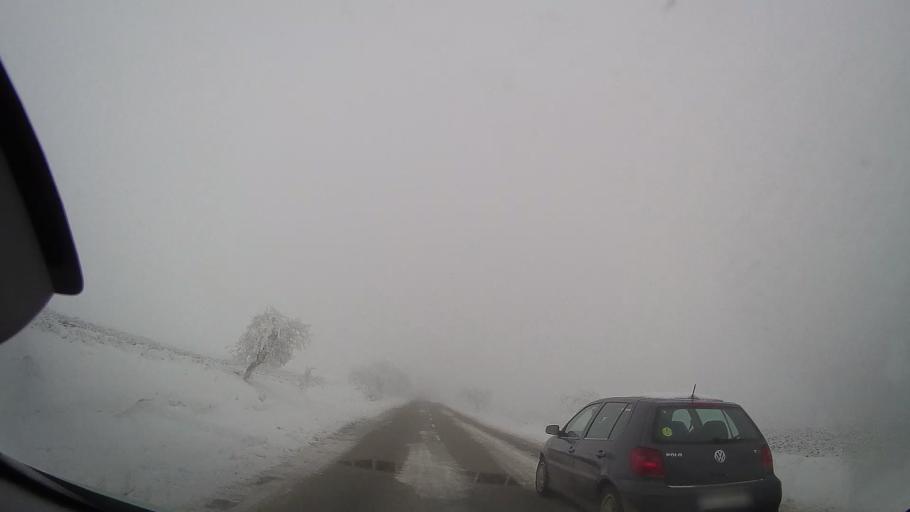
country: RO
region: Neamt
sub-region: Comuna Valea Ursului
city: Valea Ursului
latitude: 46.8281
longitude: 27.0638
